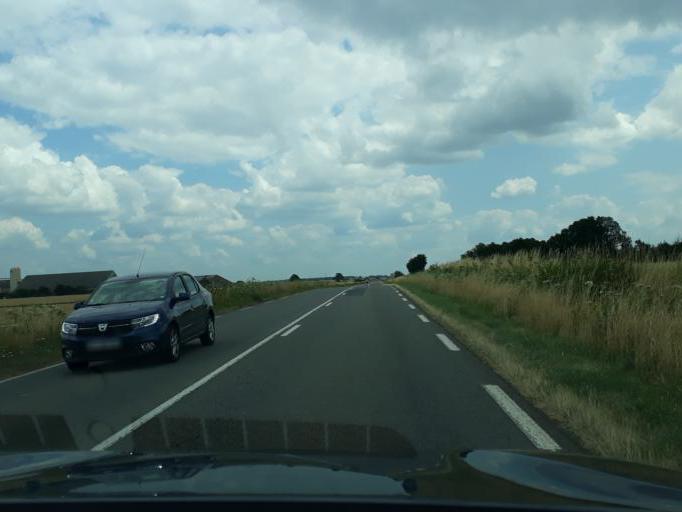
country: FR
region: Centre
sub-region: Departement du Cher
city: Avord
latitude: 47.0204
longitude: 2.6891
